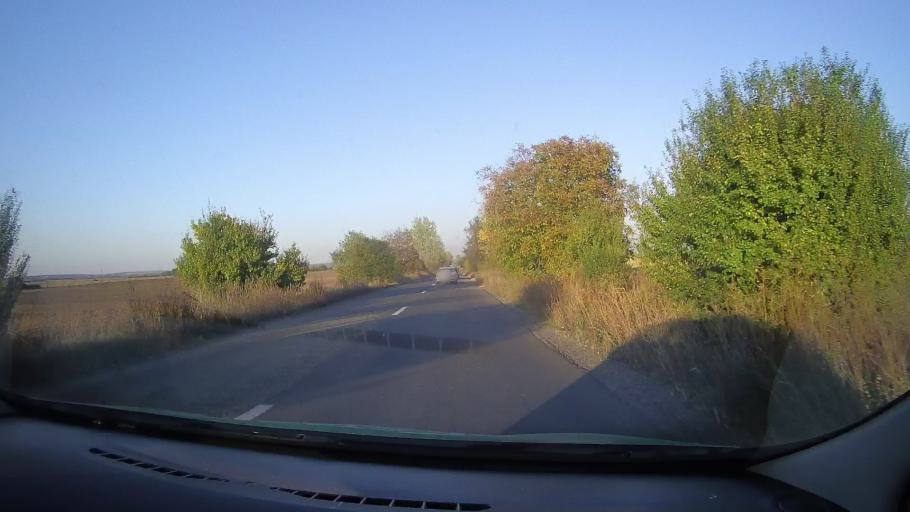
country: RO
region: Bihor
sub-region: Comuna Salard
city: Salard
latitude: 47.2031
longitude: 22.0117
